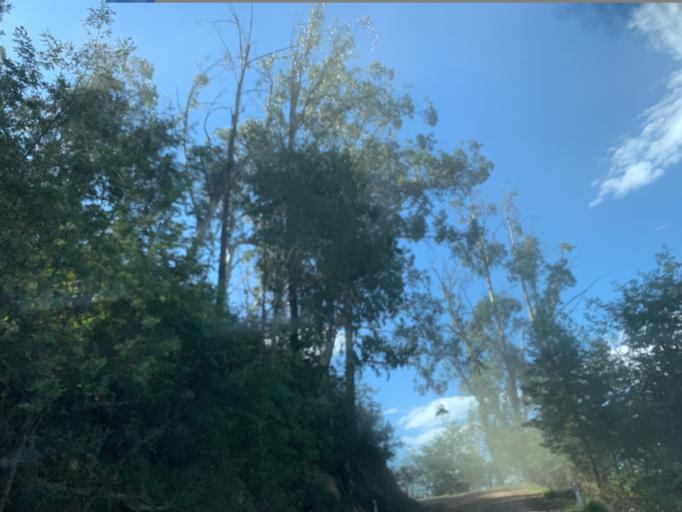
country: AU
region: Victoria
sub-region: Mansfield
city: Mansfield
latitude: -37.0979
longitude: 146.4983
